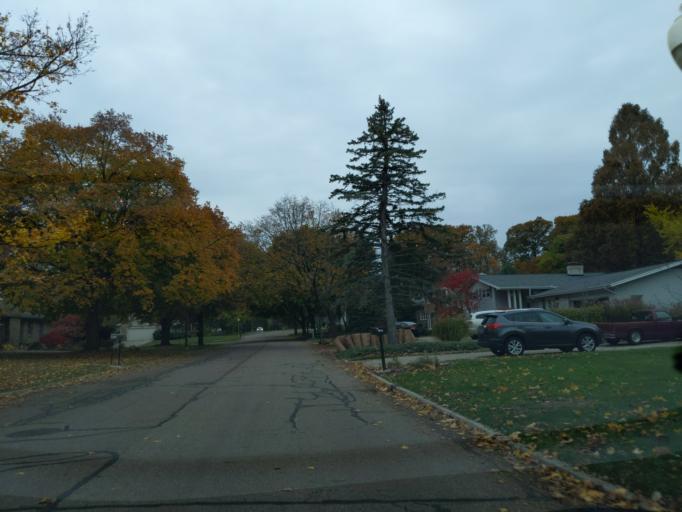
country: US
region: Michigan
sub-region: Ingham County
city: Edgemont Park
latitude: 42.7128
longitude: -84.5897
